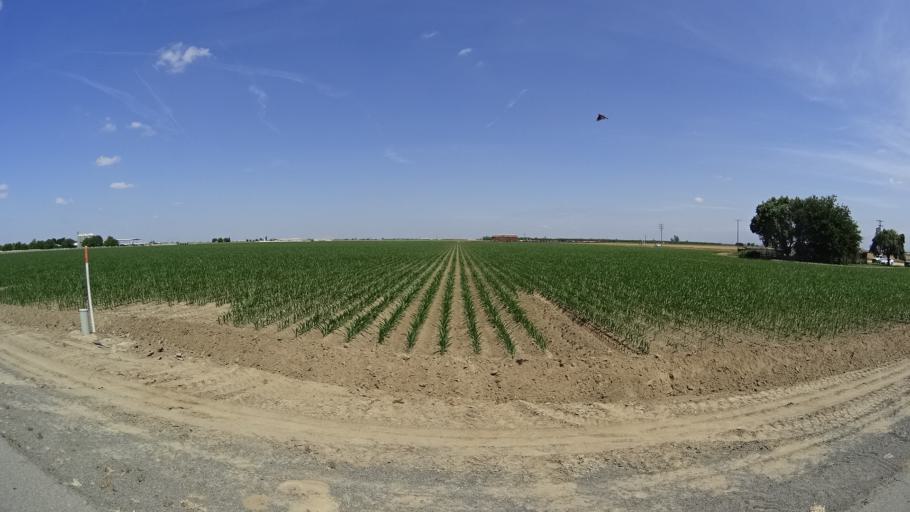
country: US
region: California
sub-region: Tulare County
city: Goshen
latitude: 36.2979
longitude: -119.4842
